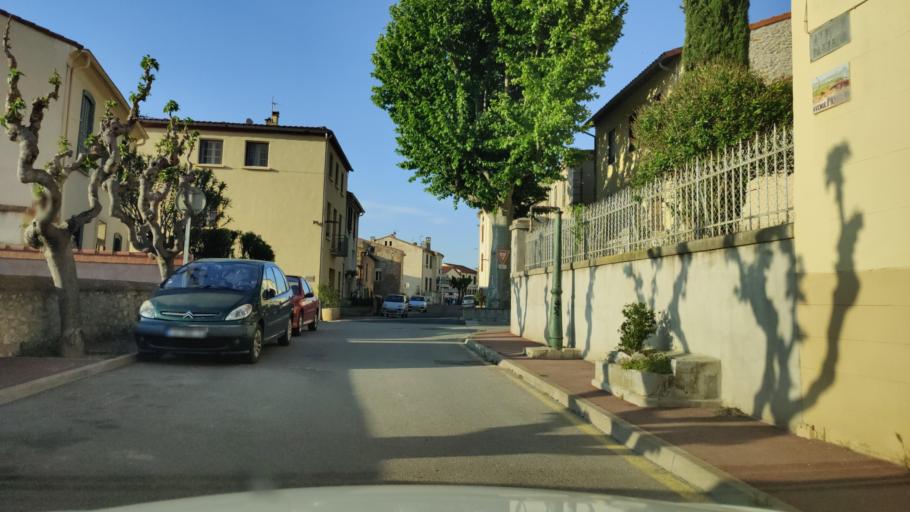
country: FR
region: Languedoc-Roussillon
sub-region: Departement des Pyrenees-Orientales
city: Estagel
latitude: 42.8131
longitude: 2.7448
